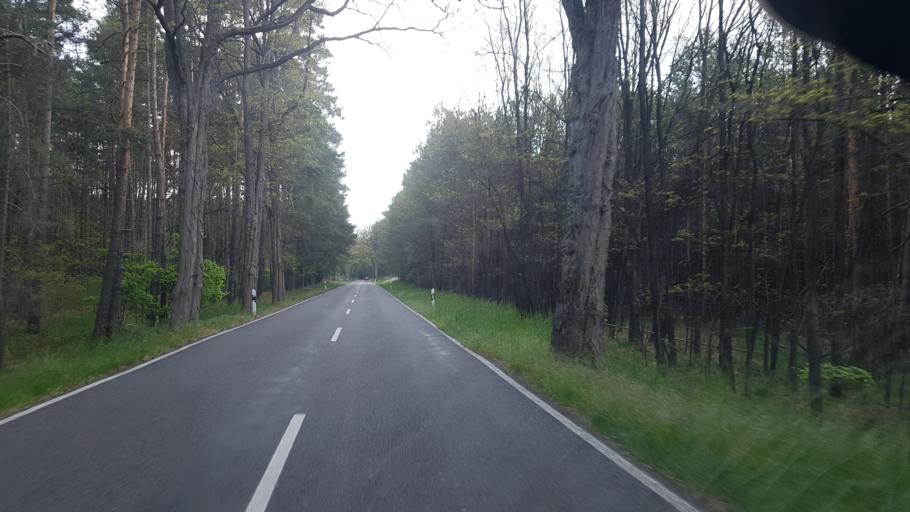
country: DE
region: Brandenburg
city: Baruth
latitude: 51.9797
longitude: 13.4662
